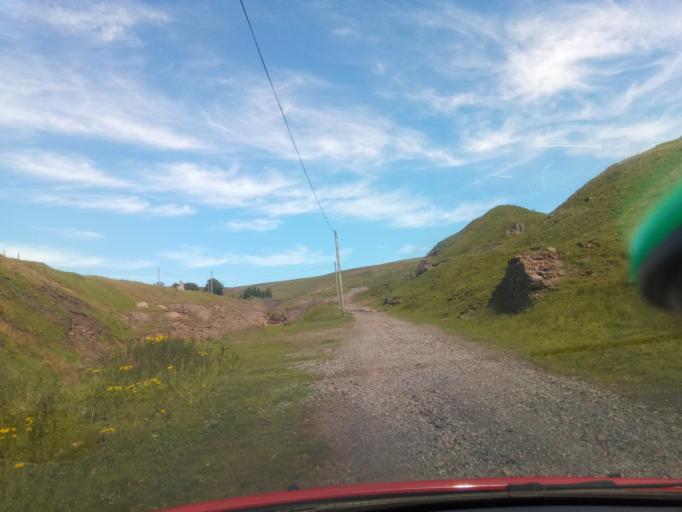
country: GB
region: England
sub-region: County Durham
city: Newbiggin
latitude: 54.7628
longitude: -2.2218
